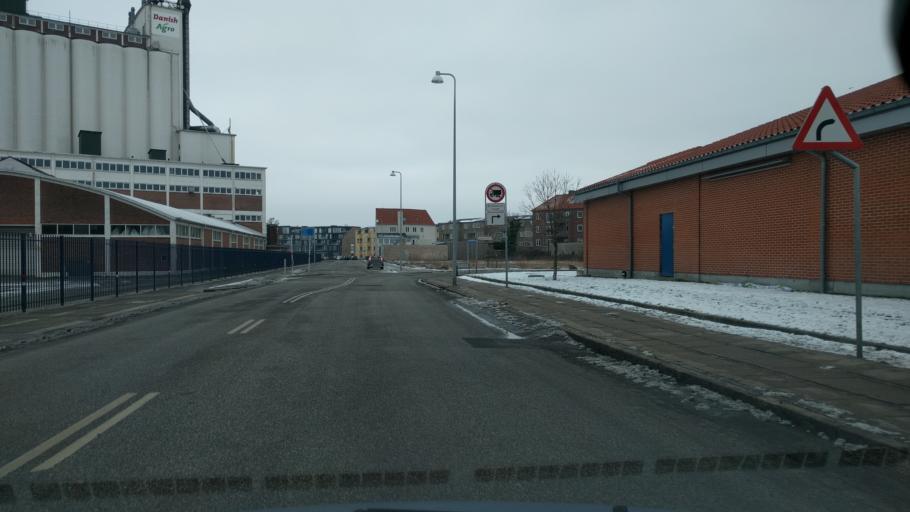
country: DK
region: Zealand
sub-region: Guldborgsund Kommune
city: Nykobing Falster
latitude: 54.7692
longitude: 11.8641
